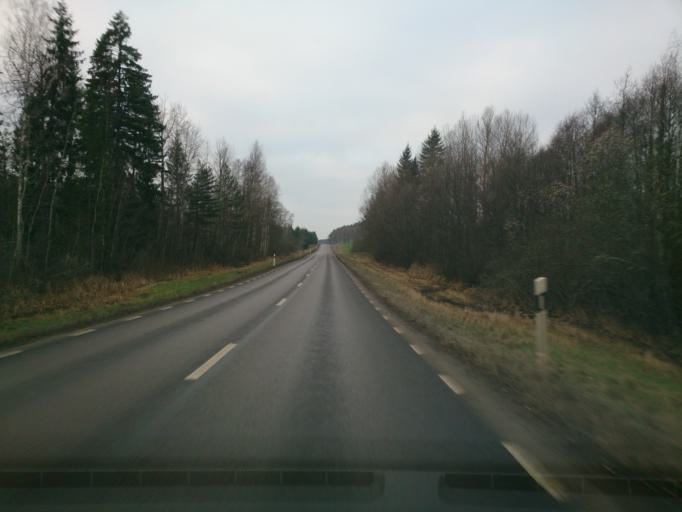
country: SE
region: OEstergoetland
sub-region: Atvidabergs Kommun
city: Atvidaberg
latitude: 58.2741
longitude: 15.9166
